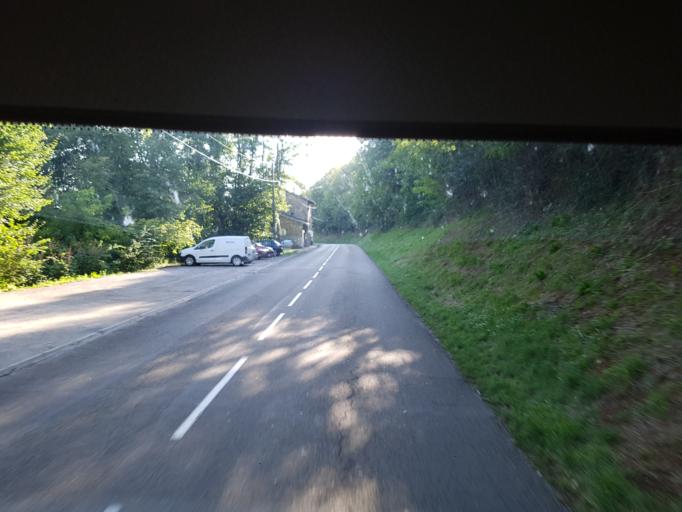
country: FR
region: Rhone-Alpes
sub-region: Departement de l'Ain
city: Neuville-sur-Ain
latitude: 46.0550
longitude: 5.3518
